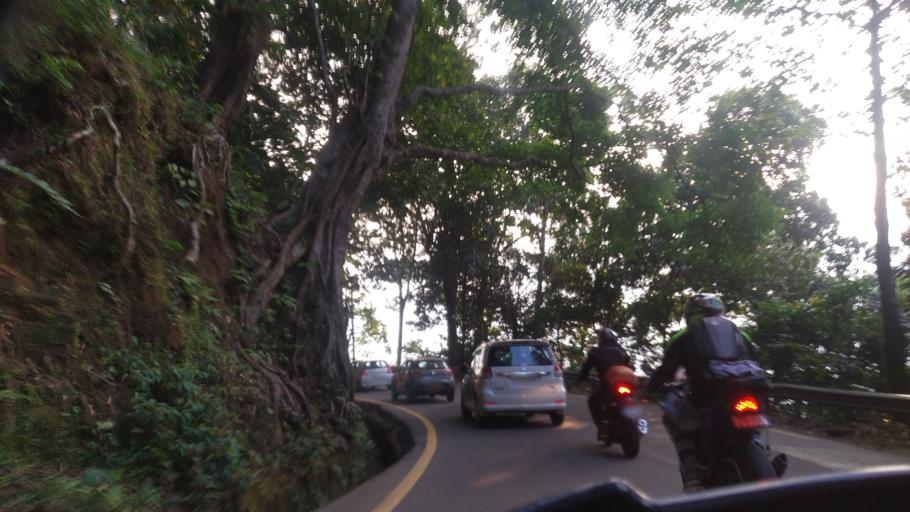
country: IN
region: Kerala
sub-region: Wayanad
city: Kalpetta
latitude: 11.5042
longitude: 76.0267
